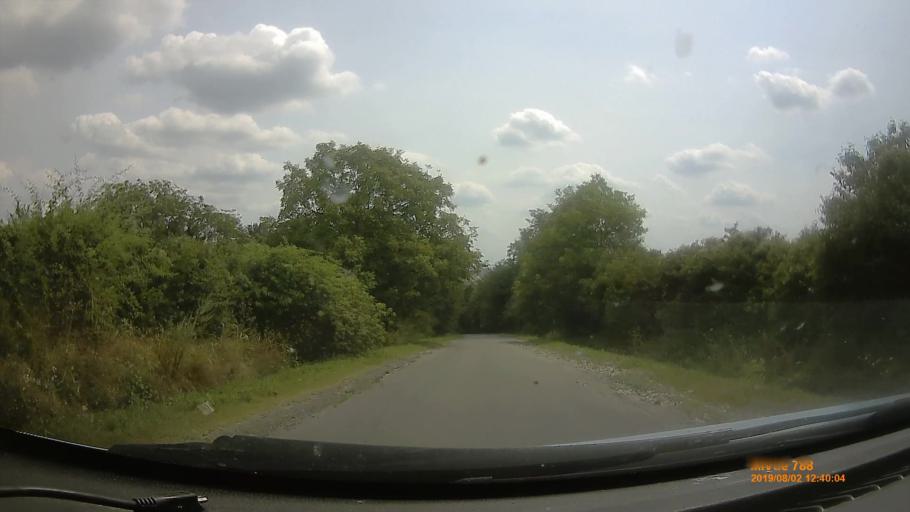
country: HU
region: Baranya
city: Buekkoesd
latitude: 46.0874
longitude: 17.9651
